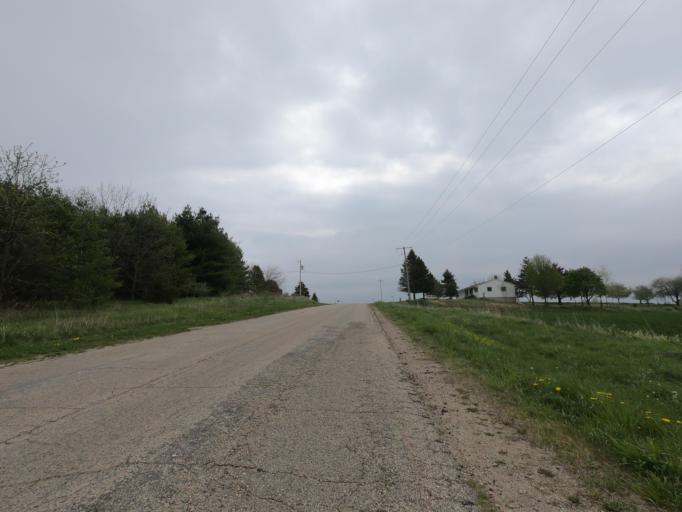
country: US
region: Wisconsin
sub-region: Jefferson County
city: Jefferson
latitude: 43.0318
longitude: -88.7835
